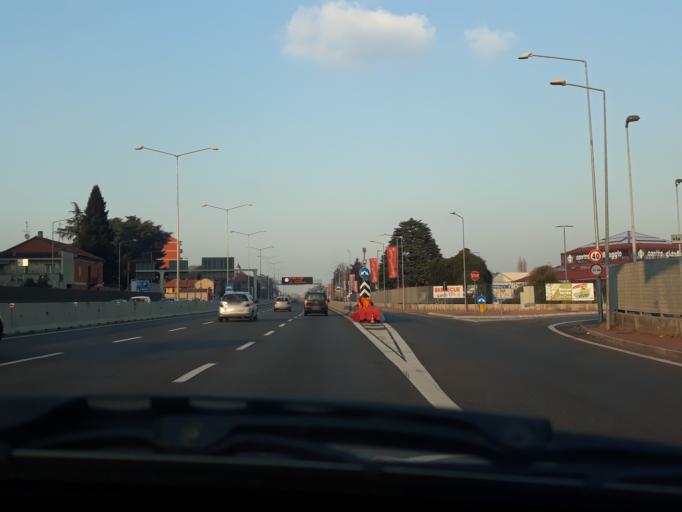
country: IT
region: Lombardy
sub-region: Citta metropolitana di Milano
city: Cinisello Balsamo
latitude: 45.5645
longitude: 9.2436
